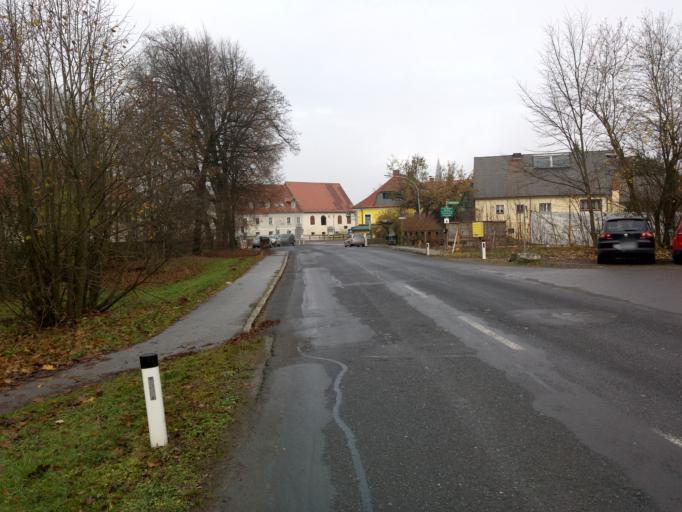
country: AT
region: Styria
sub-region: Politischer Bezirk Murtal
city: Grosslobming
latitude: 47.1834
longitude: 14.8092
